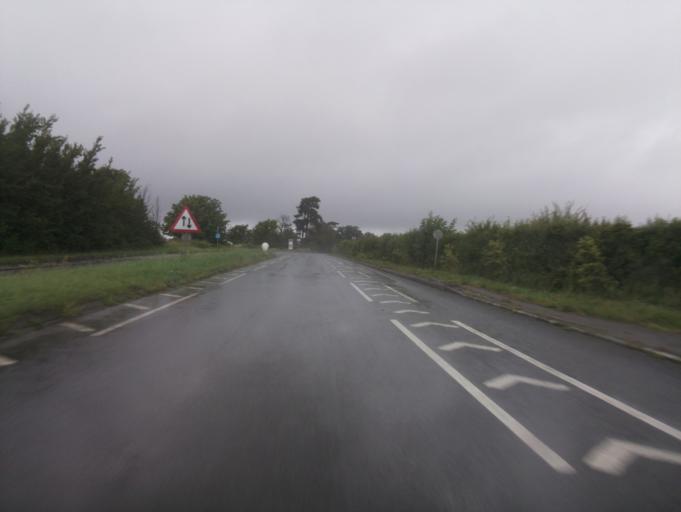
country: GB
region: England
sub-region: Gloucestershire
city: Tewkesbury
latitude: 51.9724
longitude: -2.1562
